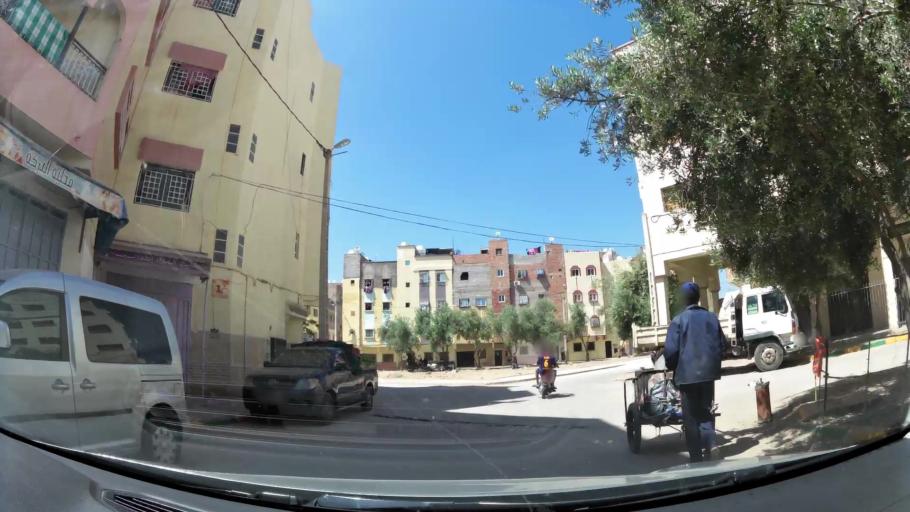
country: MA
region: Fes-Boulemane
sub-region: Fes
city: Fes
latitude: 34.0132
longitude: -5.0260
